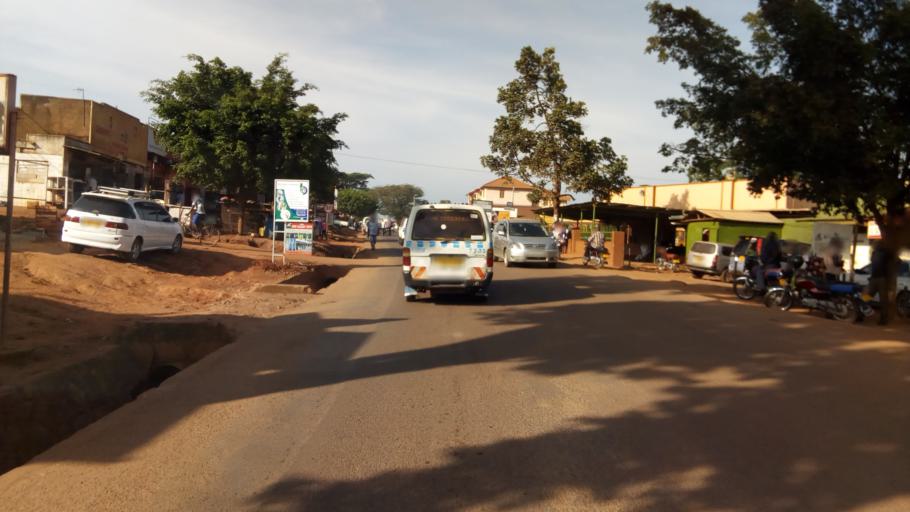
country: UG
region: Central Region
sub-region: Wakiso District
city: Kireka
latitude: 0.3209
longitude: 32.6352
